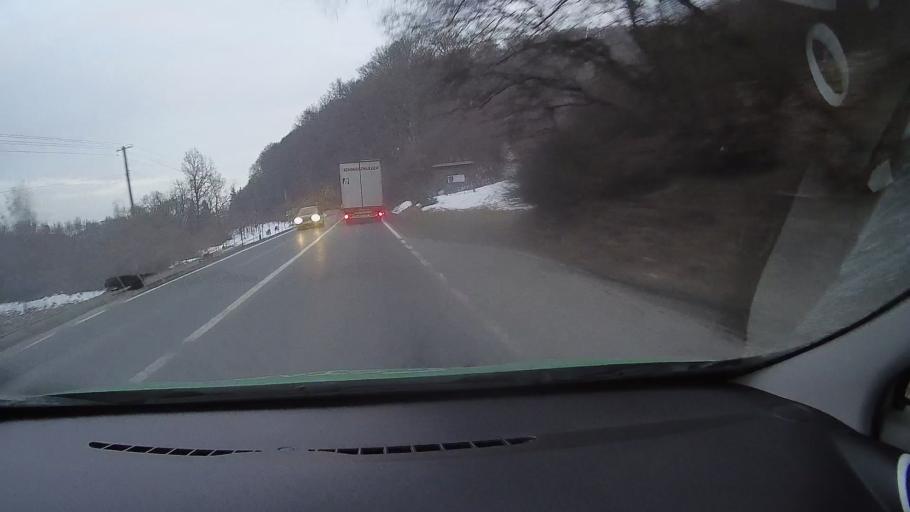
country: RO
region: Harghita
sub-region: Municipiul Odorheiu Secuiesc
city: Odorheiu Secuiesc
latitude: 46.3336
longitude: 25.2716
